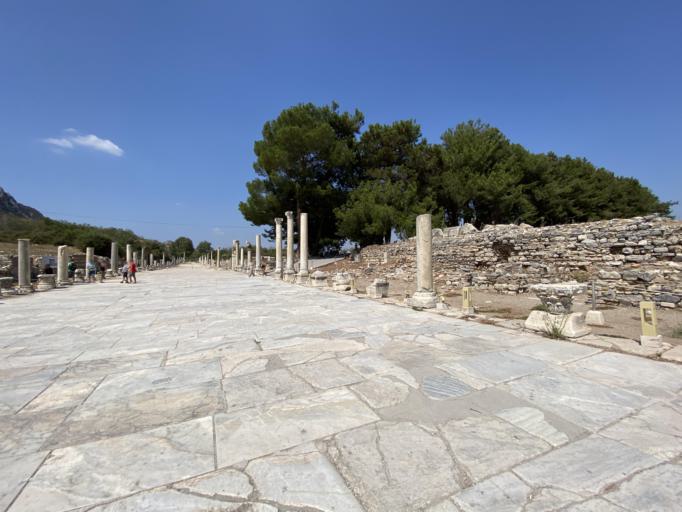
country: TR
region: Izmir
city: Selcuk
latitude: 37.9417
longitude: 27.3415
